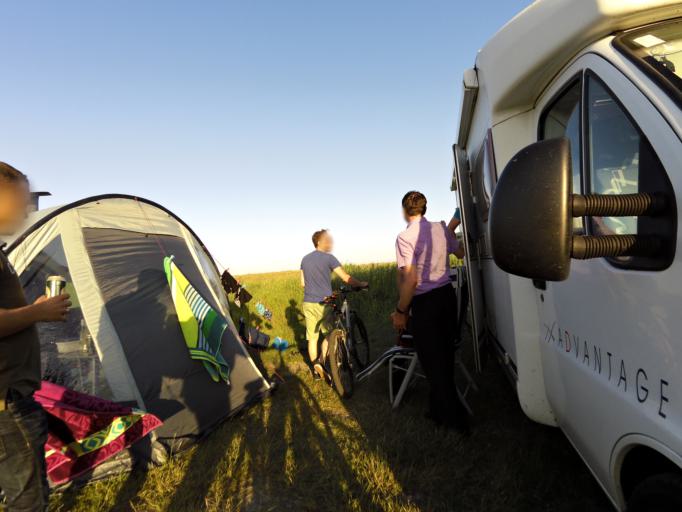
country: DE
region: Lower Saxony
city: Padingbuttel
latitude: 53.7403
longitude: 8.5177
